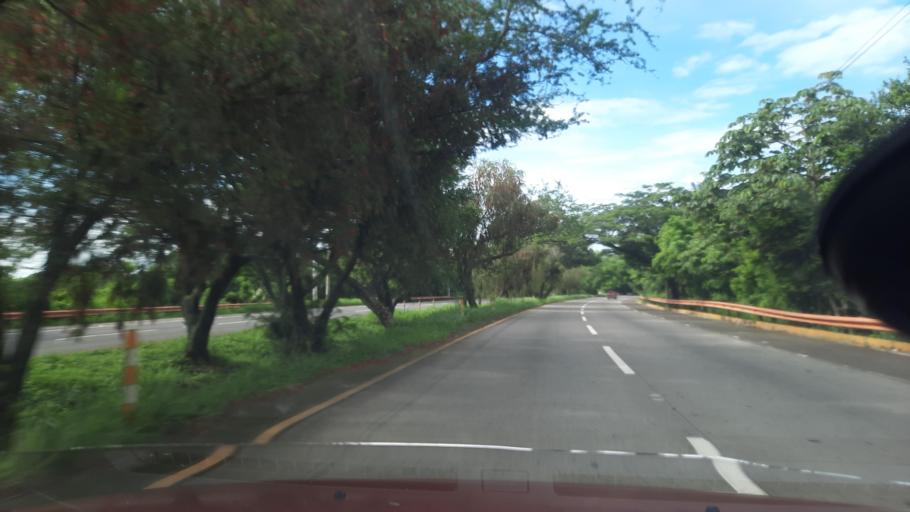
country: SV
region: La Paz
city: Olocuilta
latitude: 13.5421
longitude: -89.1114
